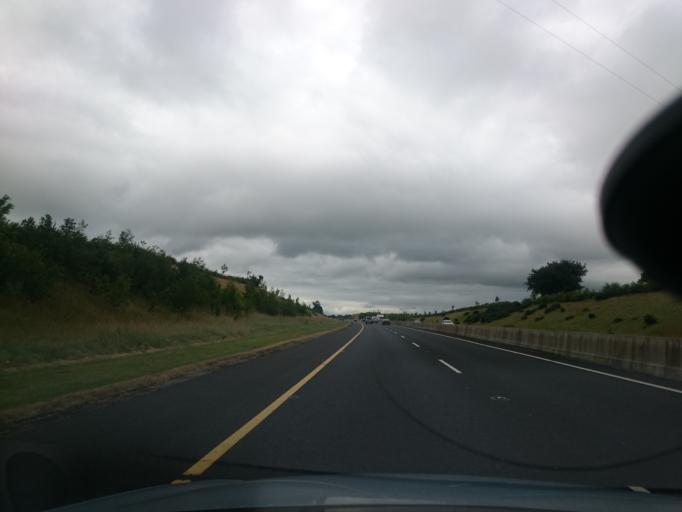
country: IE
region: Leinster
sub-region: Kildare
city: Old Kilcullen
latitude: 53.0665
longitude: -6.7640
